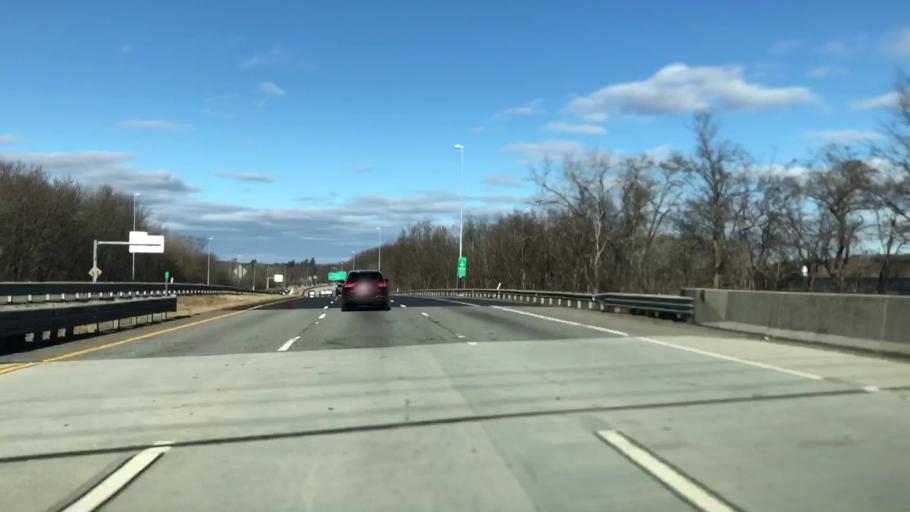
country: US
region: Massachusetts
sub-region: Worcester County
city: Auburn
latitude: 42.2226
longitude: -71.8270
